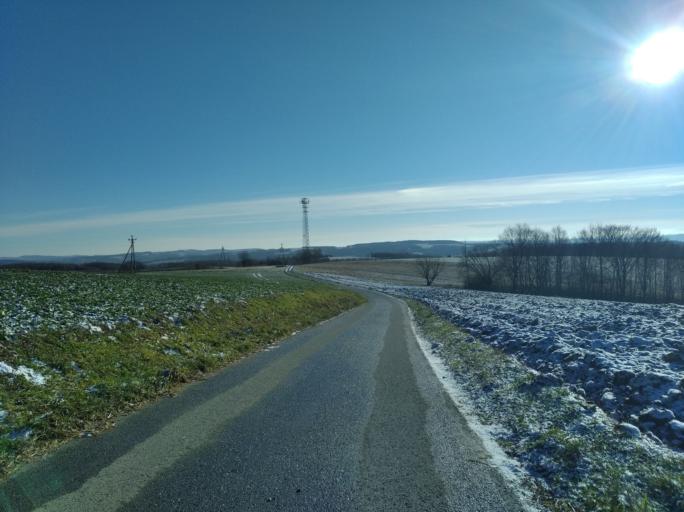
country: PL
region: Subcarpathian Voivodeship
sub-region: Powiat ropczycko-sedziszowski
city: Iwierzyce
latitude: 49.9520
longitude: 21.7604
